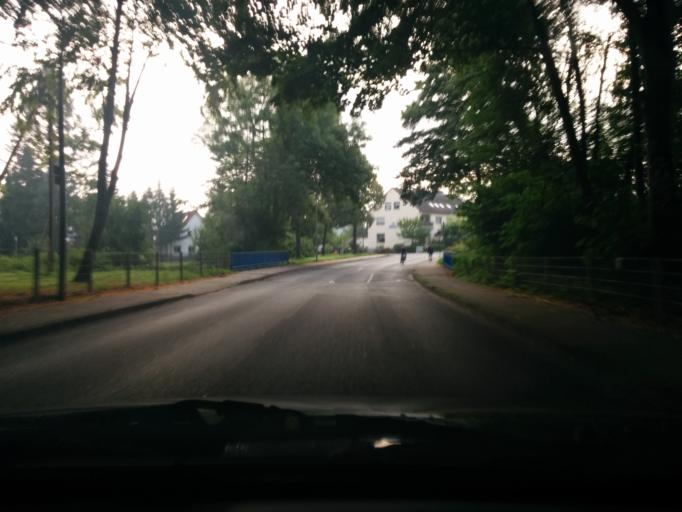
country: DE
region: North Rhine-Westphalia
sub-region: Regierungsbezirk Detmold
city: Bielefeld
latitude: 52.0058
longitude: 8.5818
